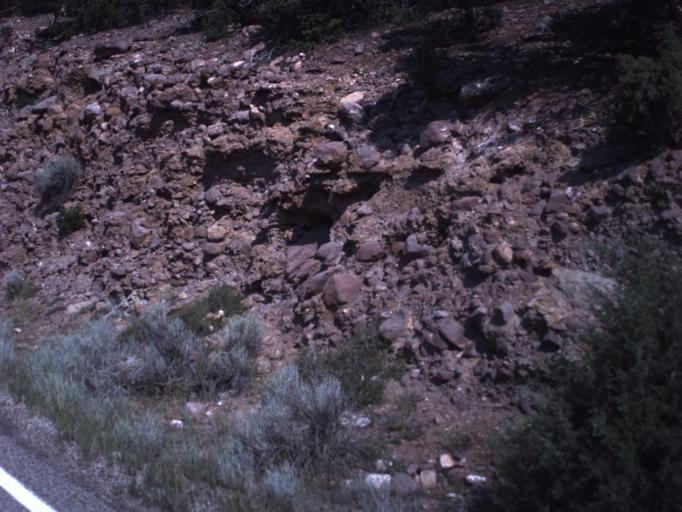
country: US
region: Utah
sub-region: Daggett County
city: Manila
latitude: 40.9135
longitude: -109.4271
